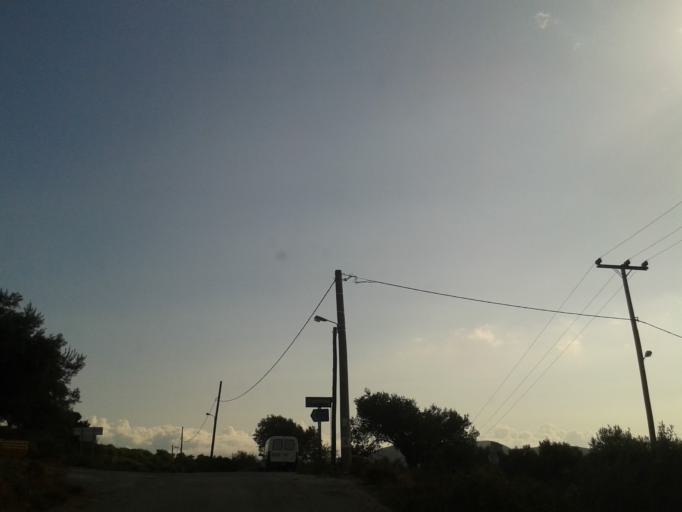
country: GR
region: Attica
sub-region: Nomarchia Anatolikis Attikis
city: Grammatiko
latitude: 38.1997
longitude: 23.9770
